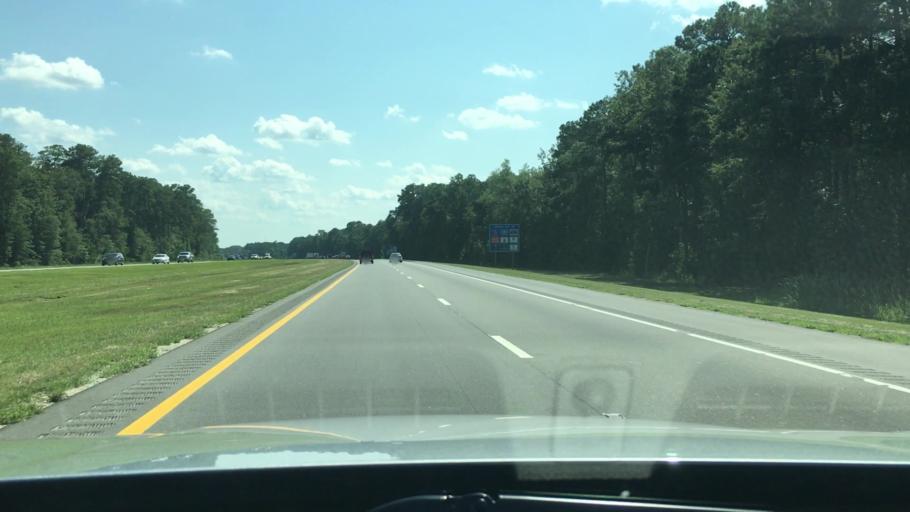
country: US
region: North Carolina
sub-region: Cumberland County
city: Vander
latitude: 35.0185
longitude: -78.8135
